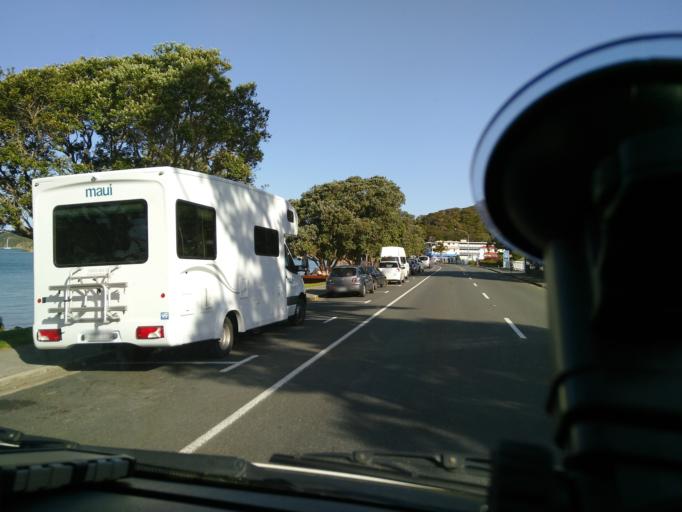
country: NZ
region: Northland
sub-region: Far North District
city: Paihia
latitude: -35.2832
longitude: 174.0938
